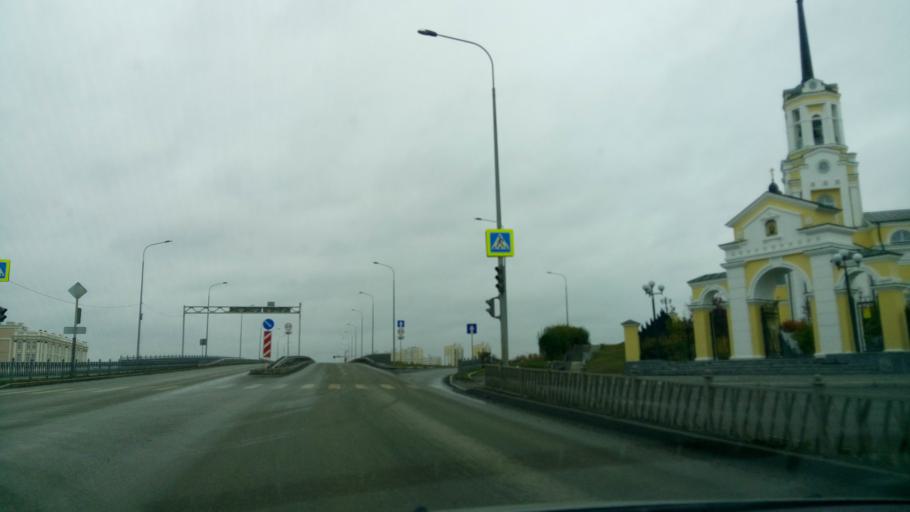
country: RU
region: Sverdlovsk
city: Verkhnyaya Pyshma
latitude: 56.9576
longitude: 60.5919
